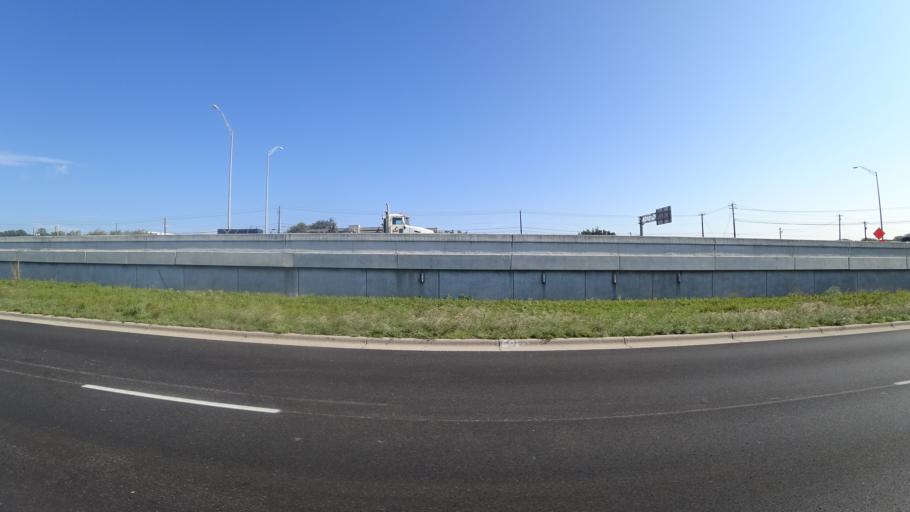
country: US
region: Texas
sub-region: Travis County
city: Austin
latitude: 30.3301
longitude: -97.6818
